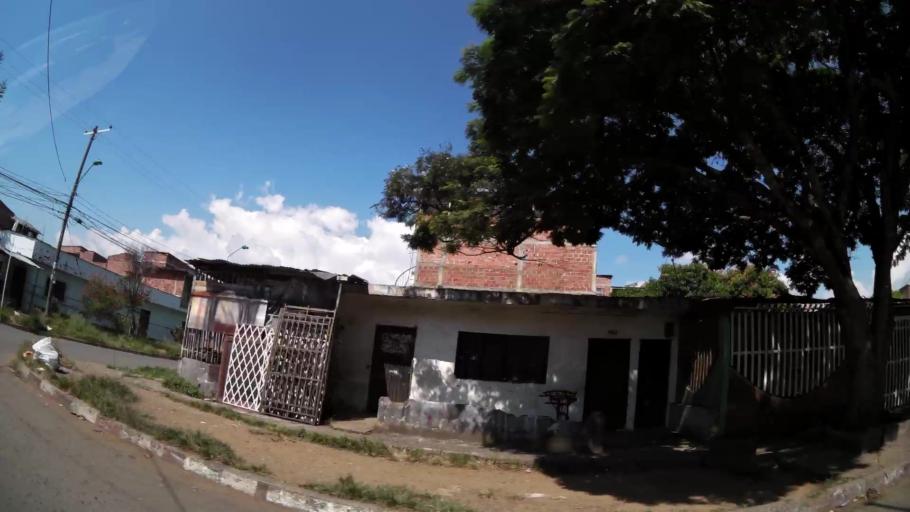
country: CO
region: Valle del Cauca
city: Cali
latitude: 3.4093
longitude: -76.5246
